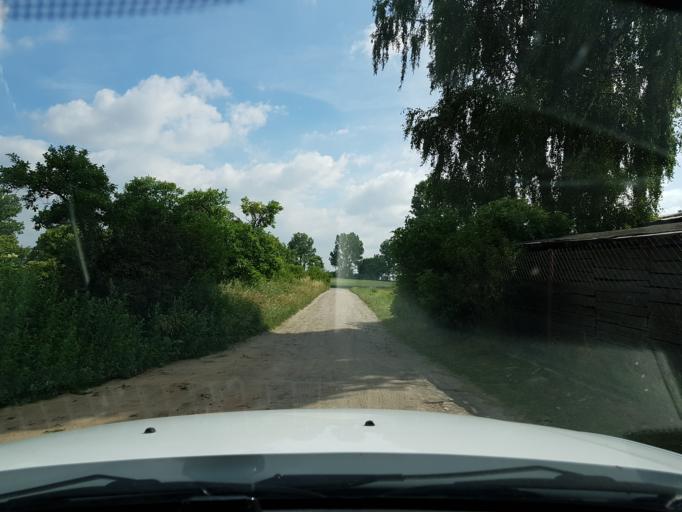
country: PL
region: West Pomeranian Voivodeship
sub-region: Powiat gryfinski
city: Banie
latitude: 53.1273
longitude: 14.5964
